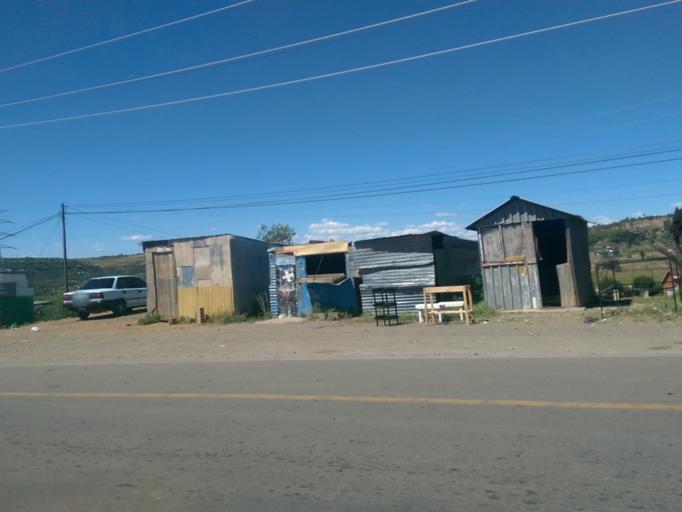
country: LS
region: Maseru
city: Maseru
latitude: -29.4053
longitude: 27.5621
